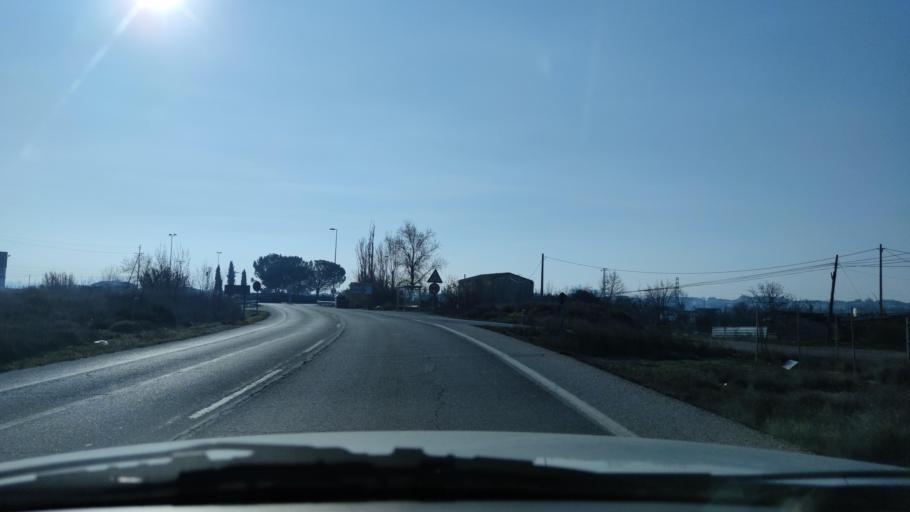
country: ES
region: Catalonia
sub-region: Provincia de Lleida
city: Lleida
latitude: 41.6473
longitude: 0.6351
